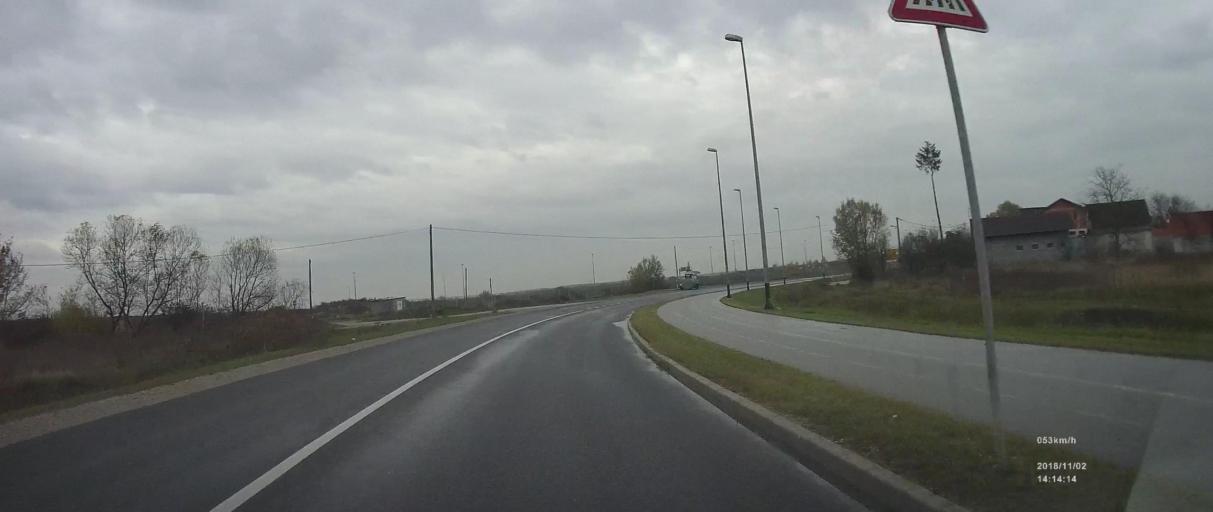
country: HR
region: Zagrebacka
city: Gradici
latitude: 45.6929
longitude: 16.0610
